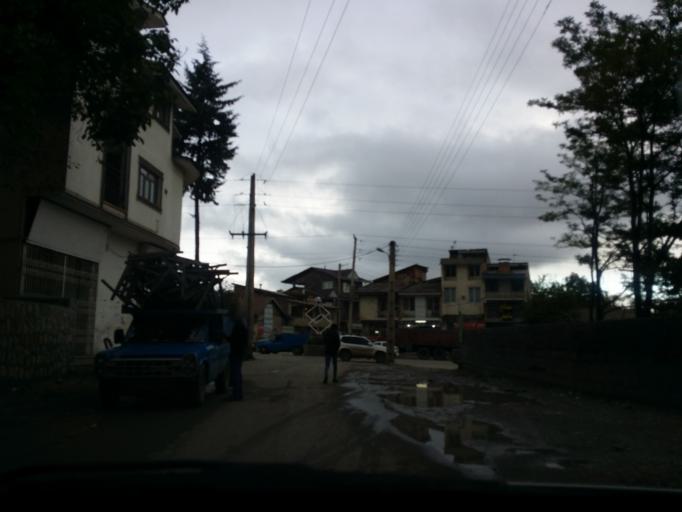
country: IR
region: Mazandaran
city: `Abbasabad
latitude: 36.5076
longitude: 51.1854
